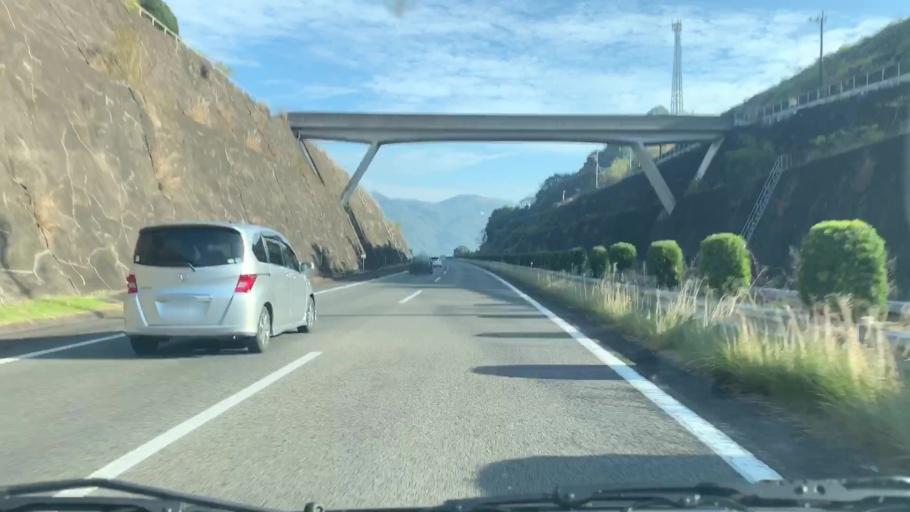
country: JP
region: Saga Prefecture
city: Takeocho-takeo
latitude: 33.2781
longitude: 130.1172
